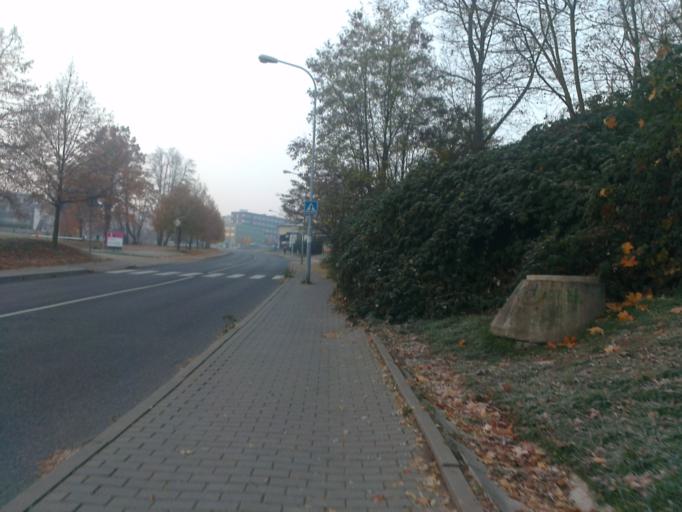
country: CZ
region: South Moravian
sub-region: Mesto Brno
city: Mokra Hora
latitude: 49.2292
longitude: 16.5768
